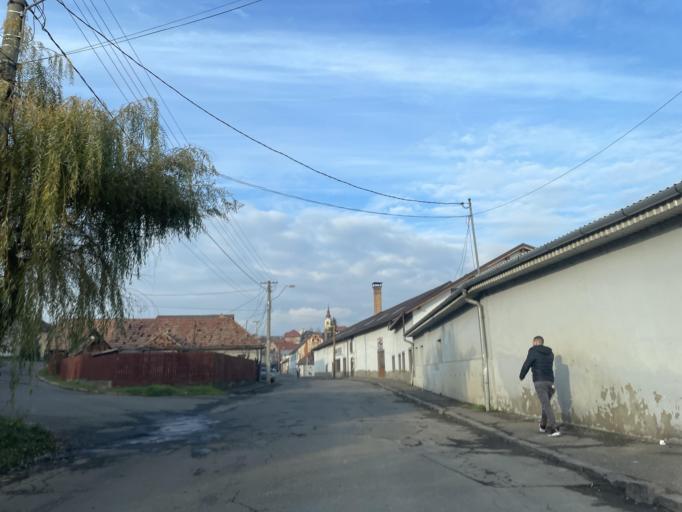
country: RO
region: Mures
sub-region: Municipiul Reghin
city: Reghin
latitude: 46.7715
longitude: 24.6976
